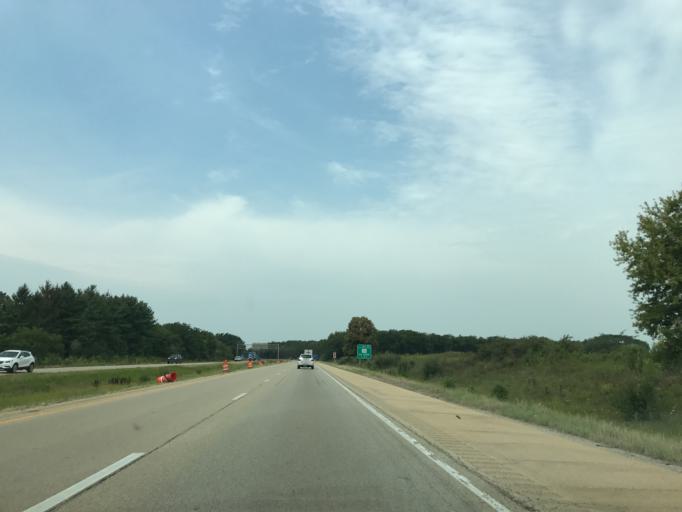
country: US
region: Illinois
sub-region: LaSalle County
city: La Salle
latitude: 41.3703
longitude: -89.0723
